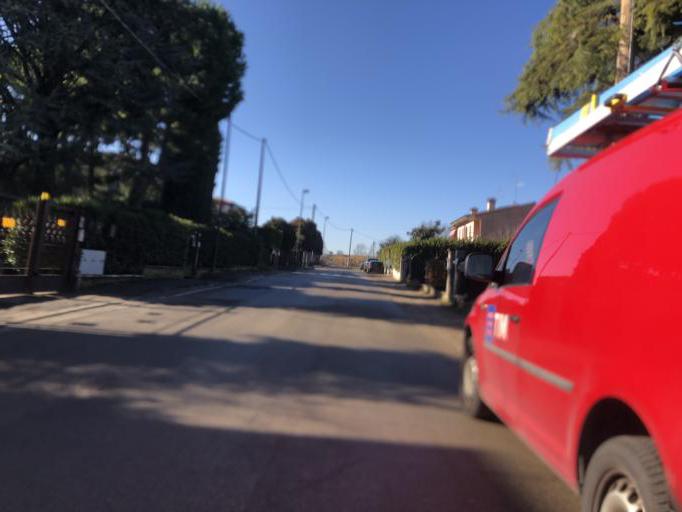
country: IT
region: Veneto
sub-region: Provincia di Verona
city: Sona
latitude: 45.4422
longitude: 10.8177
